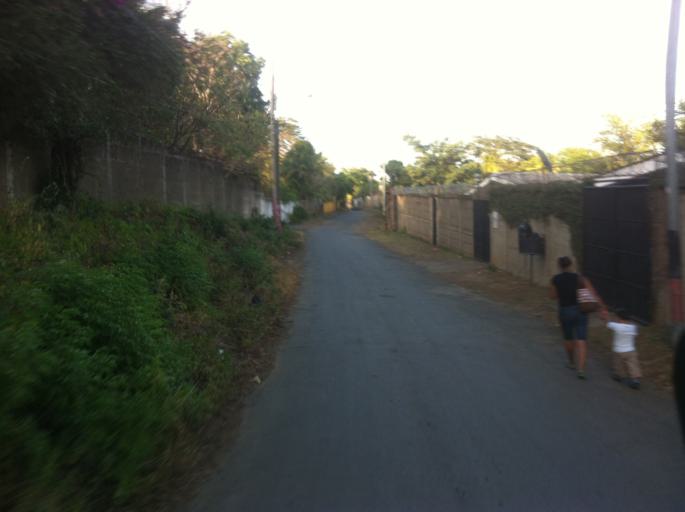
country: NI
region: Managua
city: Ciudad Sandino
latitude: 12.0988
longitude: -86.3130
